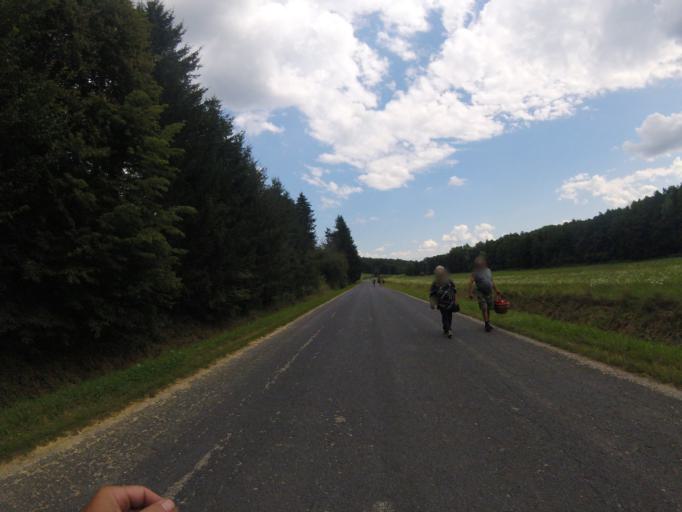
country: HU
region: Zala
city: Becsehely
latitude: 46.4975
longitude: 16.7407
